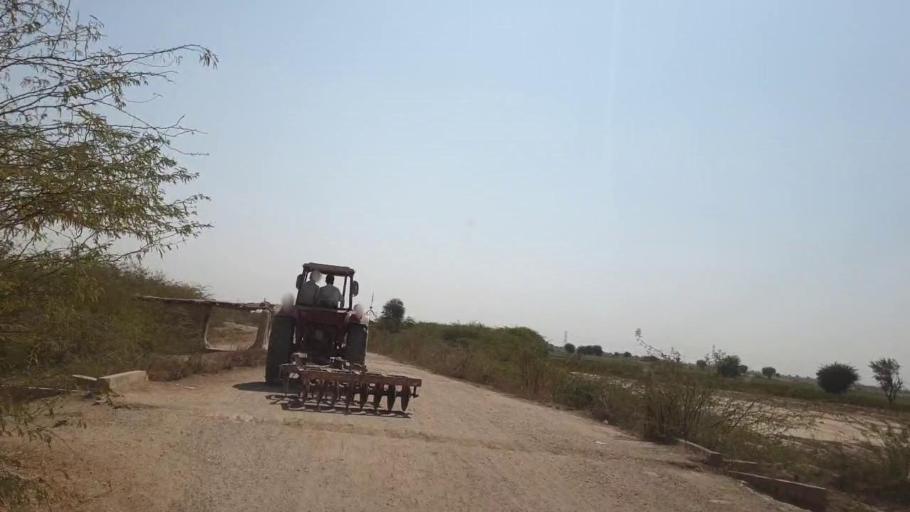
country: PK
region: Sindh
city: Kunri
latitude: 25.0818
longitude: 69.5330
